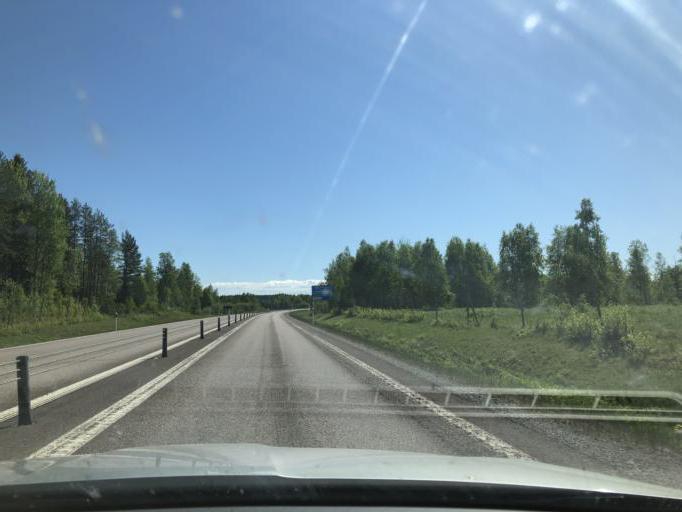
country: SE
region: Norrbotten
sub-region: Kalix Kommun
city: Rolfs
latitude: 65.8904
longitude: 22.9102
